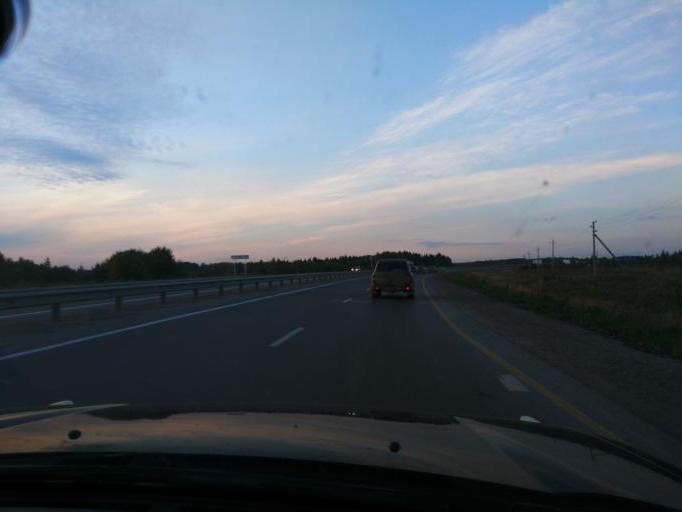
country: RU
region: Perm
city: Polazna
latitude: 58.2019
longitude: 56.4017
